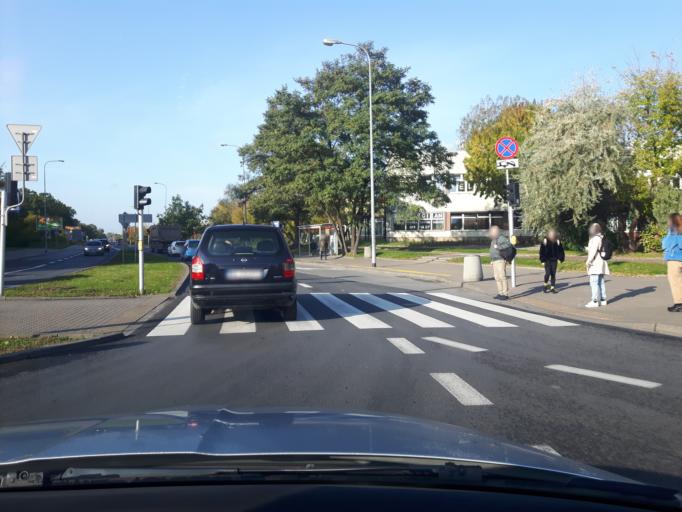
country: PL
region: Masovian Voivodeship
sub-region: Warszawa
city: Targowek
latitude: 52.2867
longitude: 21.0481
